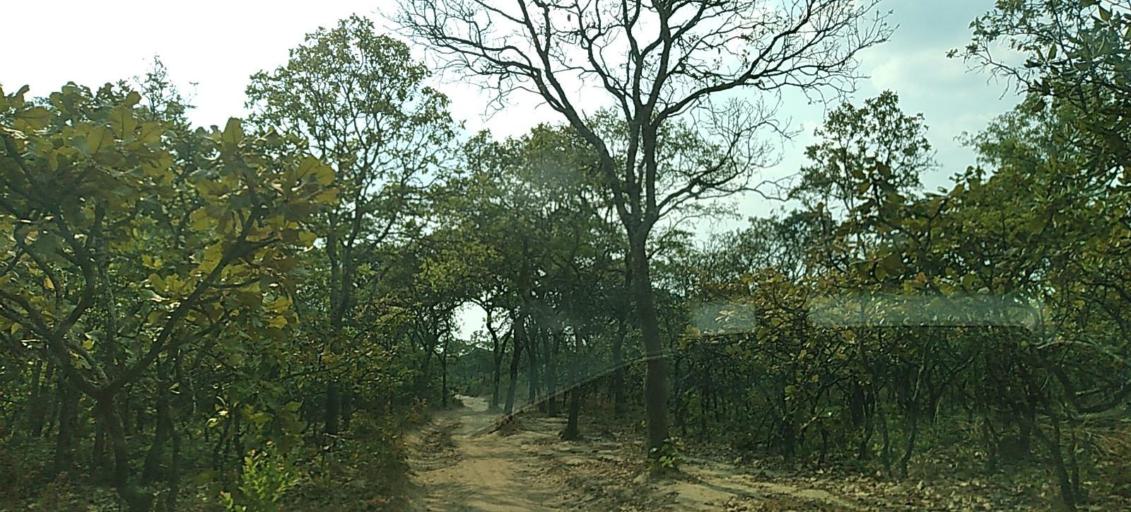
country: ZM
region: North-Western
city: Solwezi
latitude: -12.0742
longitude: 26.2343
